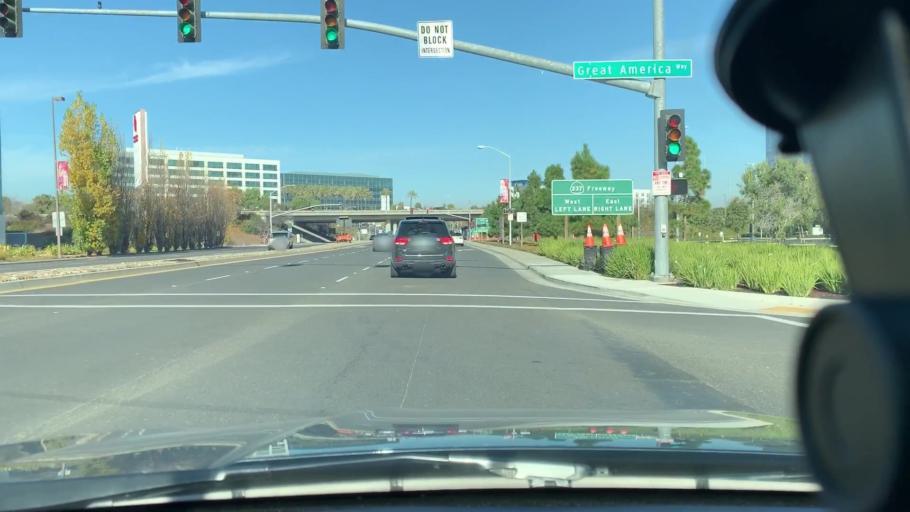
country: US
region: California
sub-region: Santa Clara County
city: Santa Clara
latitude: 37.4139
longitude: -121.9774
